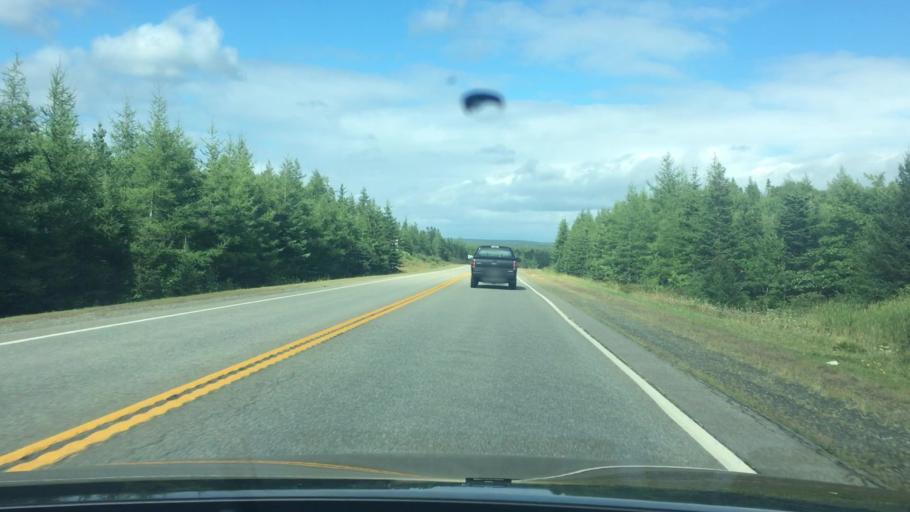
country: CA
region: Nova Scotia
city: Princeville
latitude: 45.6218
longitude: -61.0490
